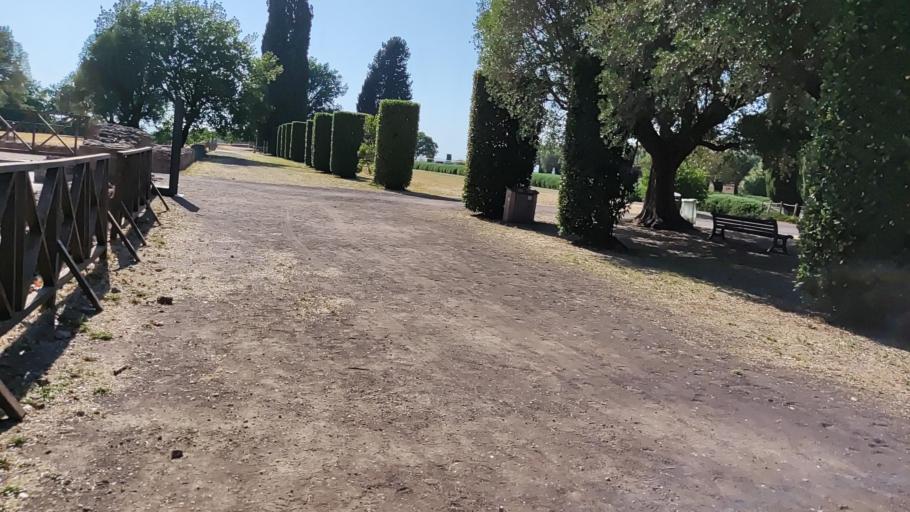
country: IT
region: Latium
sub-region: Citta metropolitana di Roma Capitale
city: Villa Adriana
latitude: 41.9414
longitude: 12.7750
